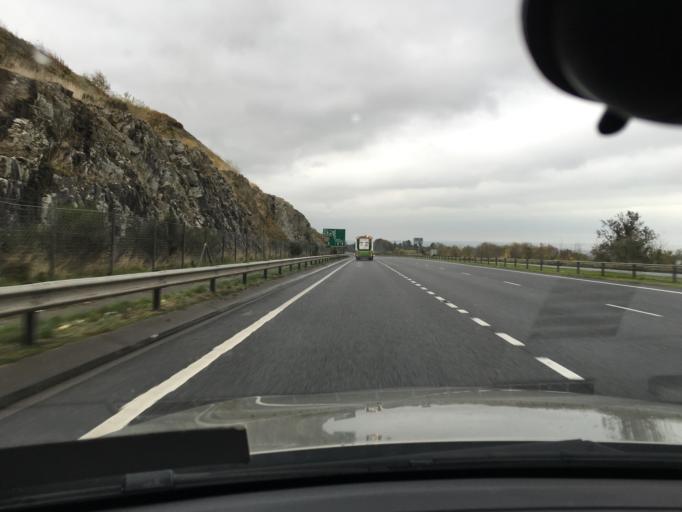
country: GB
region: Northern Ireland
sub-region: Newry and Mourne District
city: Newry
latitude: 54.1443
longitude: -6.3433
